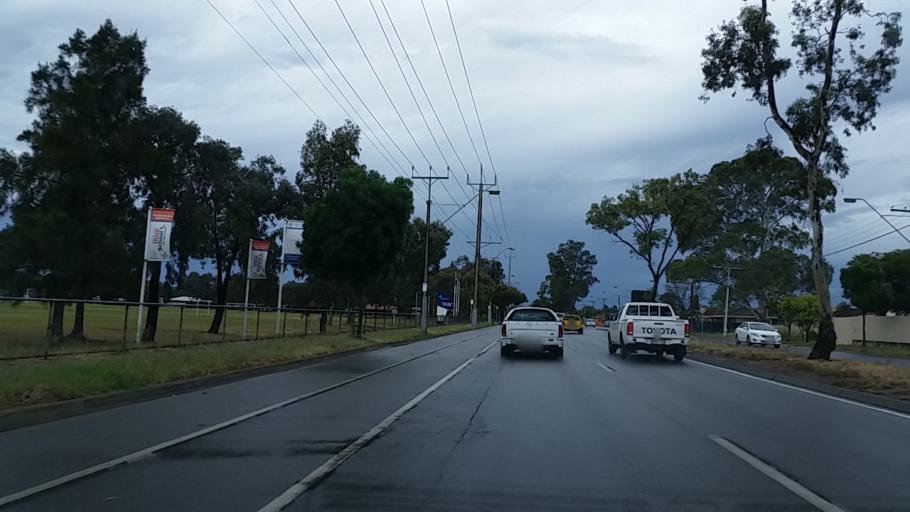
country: AU
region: South Australia
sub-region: Salisbury
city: Salisbury
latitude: -34.7870
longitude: 138.6193
